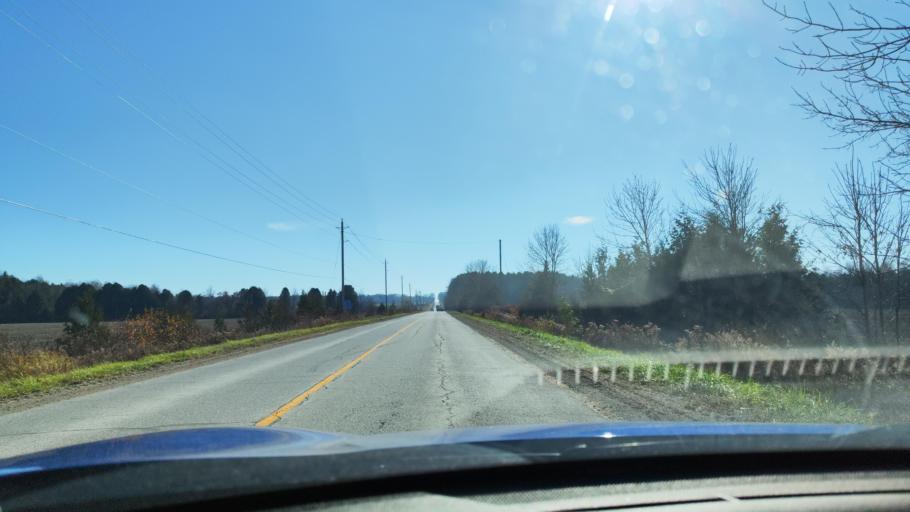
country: CA
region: Ontario
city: Wasaga Beach
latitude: 44.4688
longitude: -80.0058
